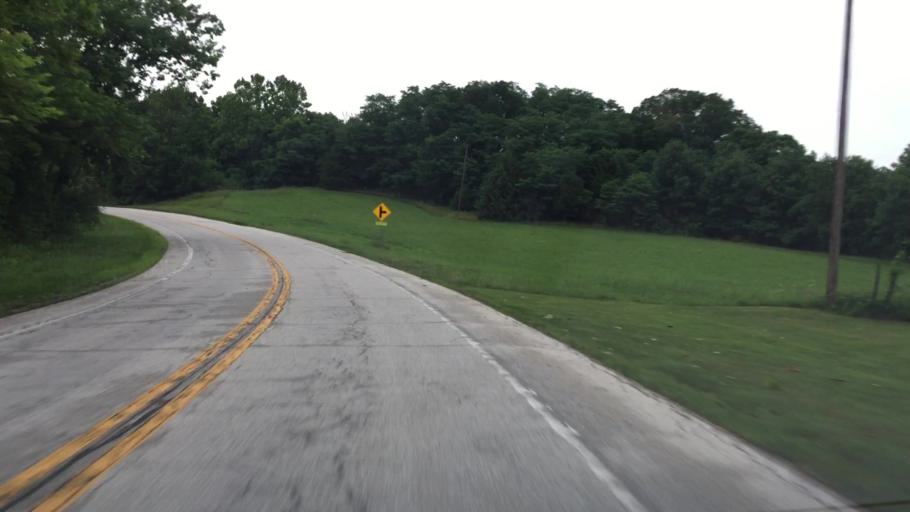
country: US
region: Illinois
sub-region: Hancock County
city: Nauvoo
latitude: 40.5181
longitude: -91.3587
